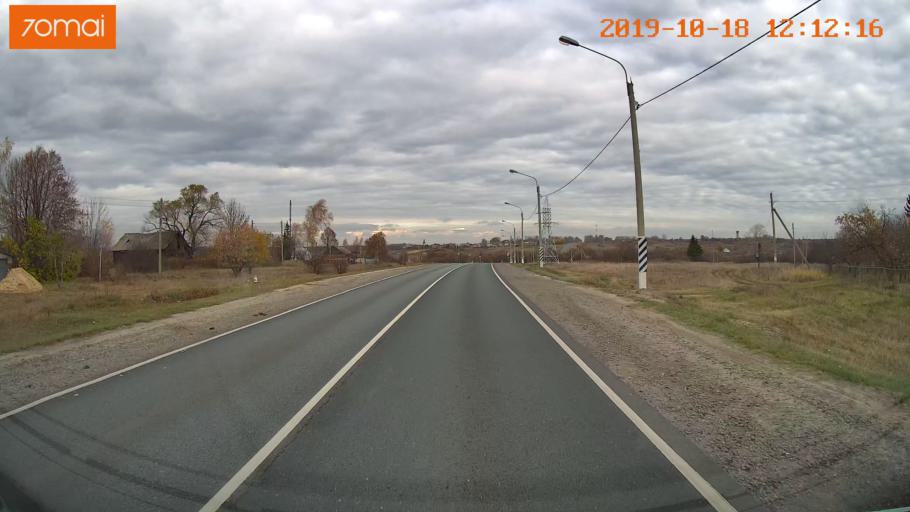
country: RU
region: Rjazan
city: Zakharovo
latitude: 54.4100
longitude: 39.3566
